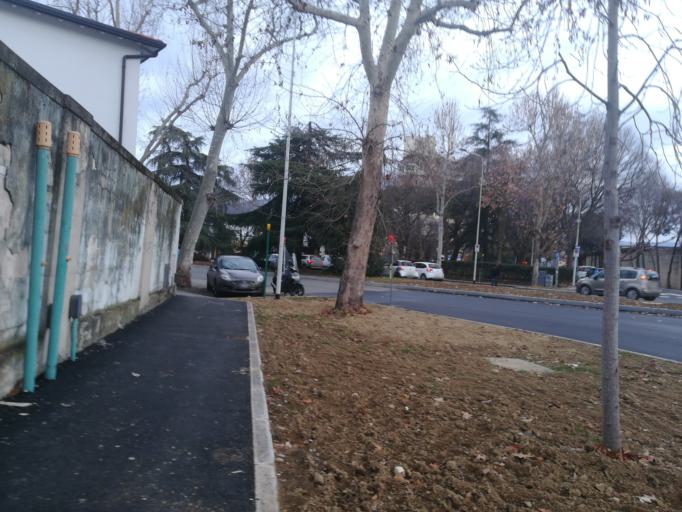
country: IT
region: Tuscany
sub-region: Province of Florence
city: Florence
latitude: 43.8020
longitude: 11.2304
